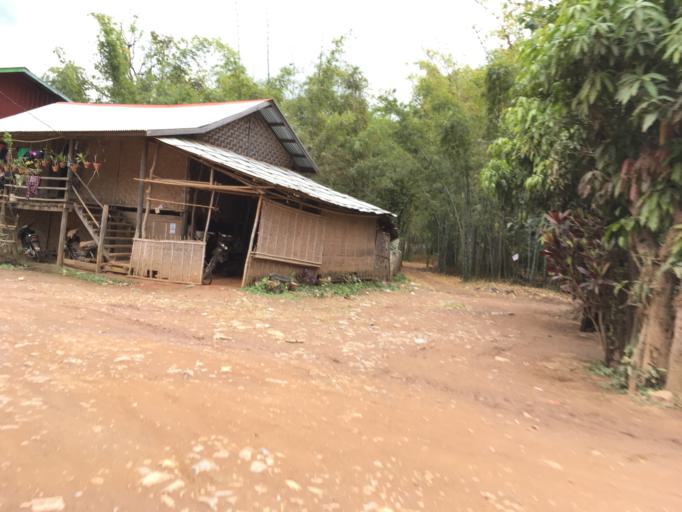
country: MM
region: Shan
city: Taunggyi
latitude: 20.6196
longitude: 96.8833
